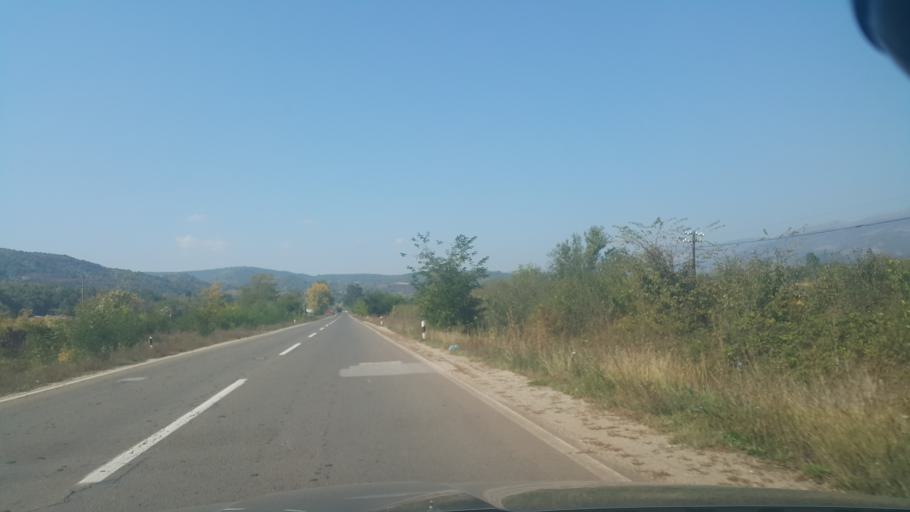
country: RS
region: Central Serbia
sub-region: Pirotski Okrug
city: Bela Palanka
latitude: 43.2290
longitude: 22.2851
